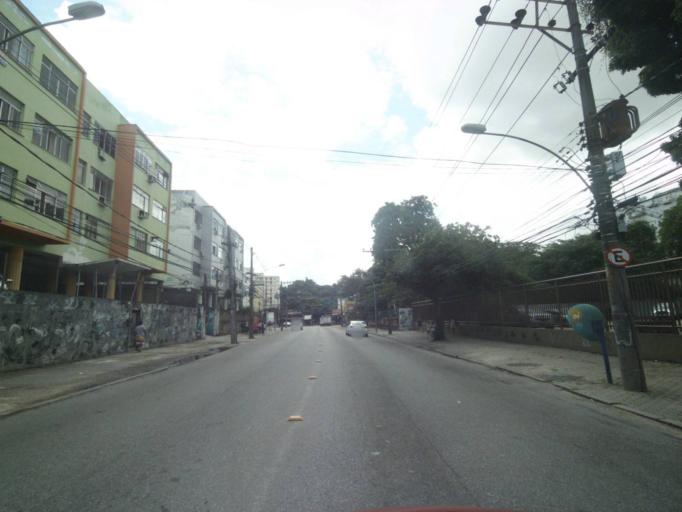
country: BR
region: Rio de Janeiro
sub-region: Sao Joao De Meriti
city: Sao Joao de Meriti
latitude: -22.9302
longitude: -43.3535
